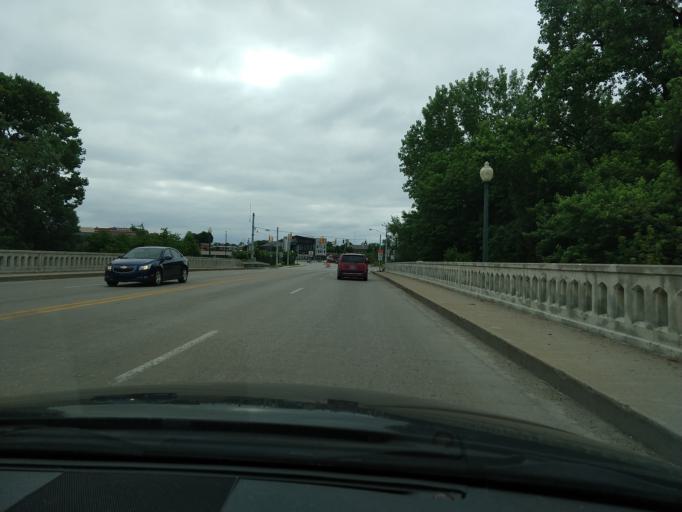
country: US
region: Indiana
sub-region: Hamilton County
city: Noblesville
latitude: 40.0459
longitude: -86.0172
